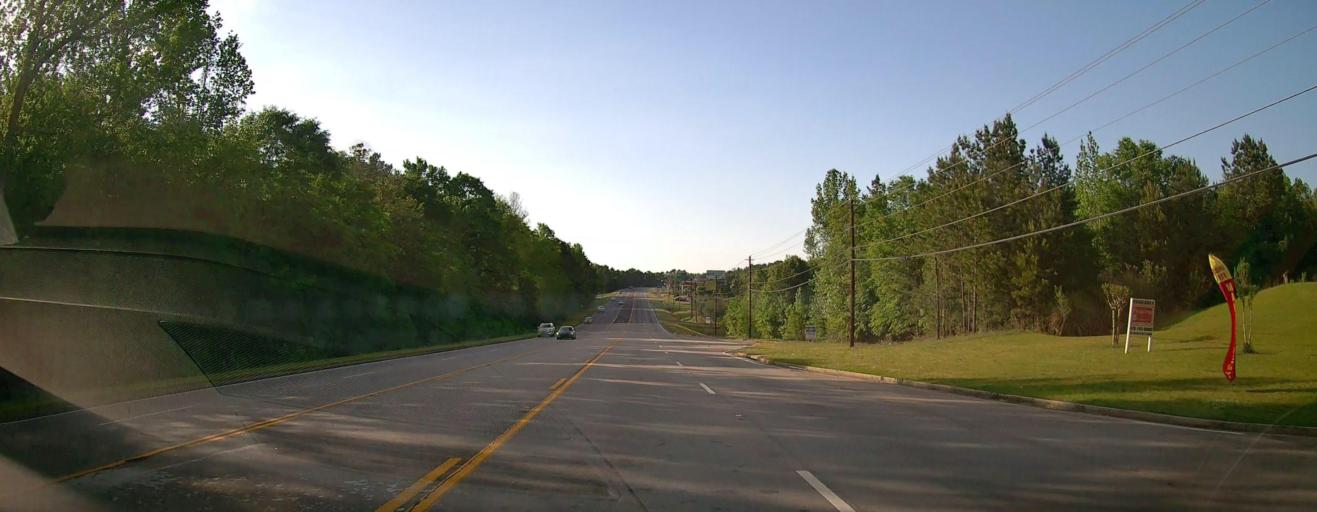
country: US
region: Georgia
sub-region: Baldwin County
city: Milledgeville
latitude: 33.1280
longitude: -83.2666
